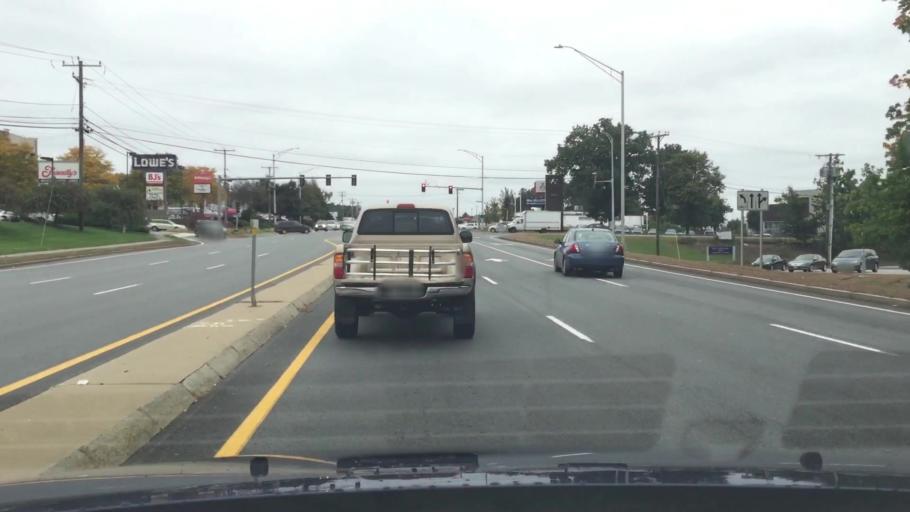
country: US
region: New Hampshire
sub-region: Hillsborough County
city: Hudson
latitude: 42.7250
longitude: -71.4455
